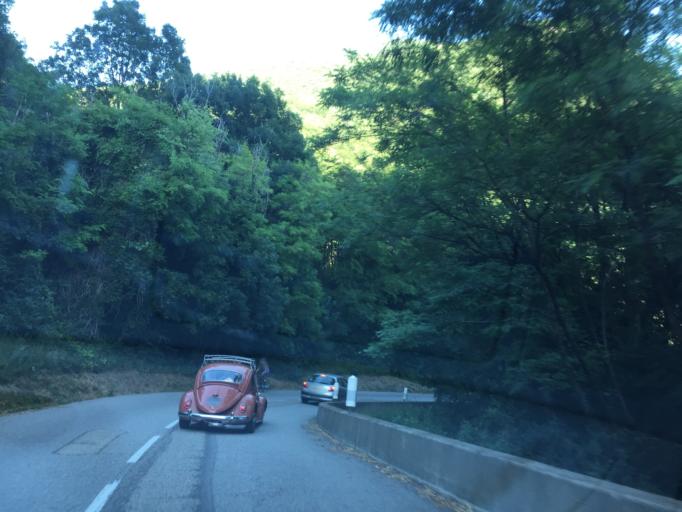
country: FR
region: Rhone-Alpes
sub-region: Departement de la Savoie
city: Challes-les-Eaux
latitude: 45.5445
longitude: 6.0059
